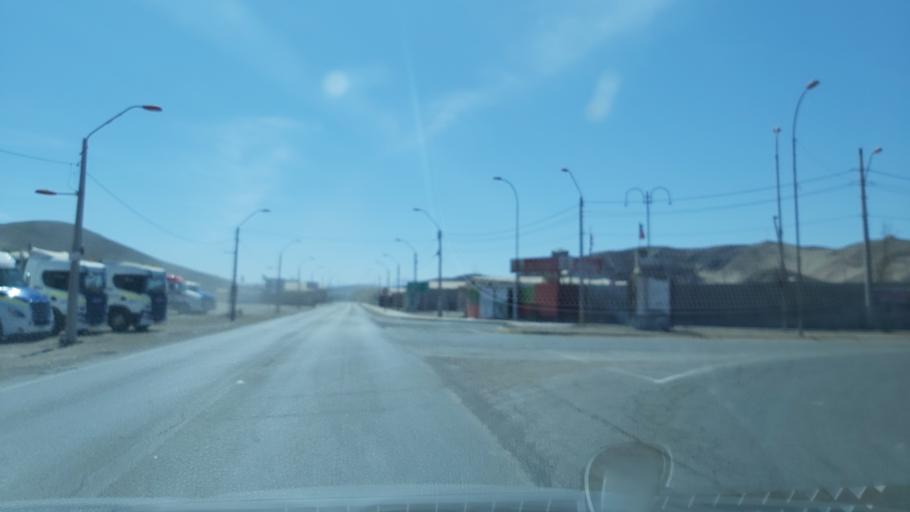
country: CL
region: Atacama
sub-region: Provincia de Chanaral
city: Diego de Almagro
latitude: -26.3915
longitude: -70.0412
